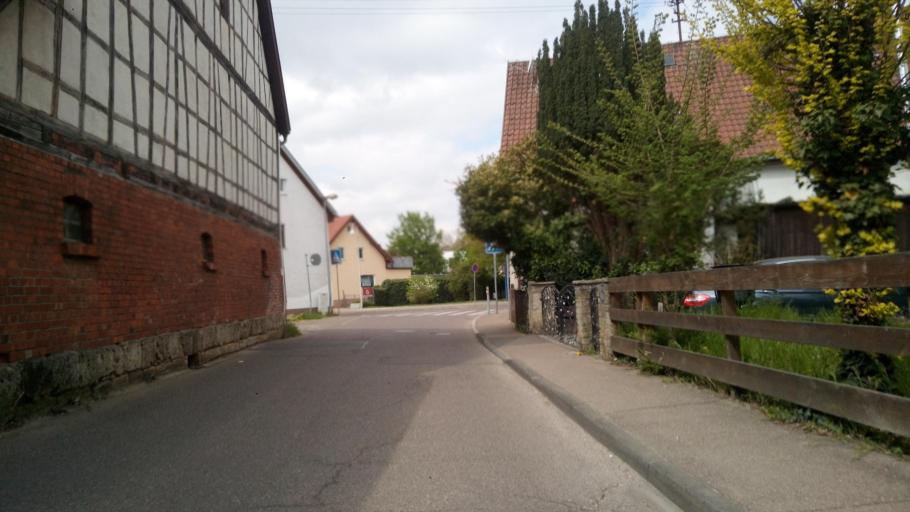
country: DE
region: Baden-Wuerttemberg
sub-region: Regierungsbezirk Stuttgart
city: Eislingen
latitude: 48.7026
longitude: 9.7100
